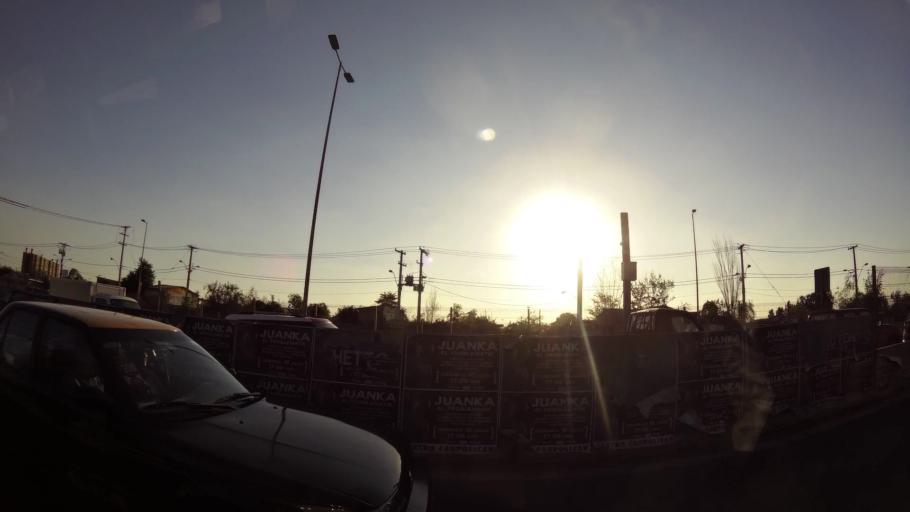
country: CL
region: Santiago Metropolitan
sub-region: Provincia de Santiago
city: La Pintana
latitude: -33.5388
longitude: -70.6205
